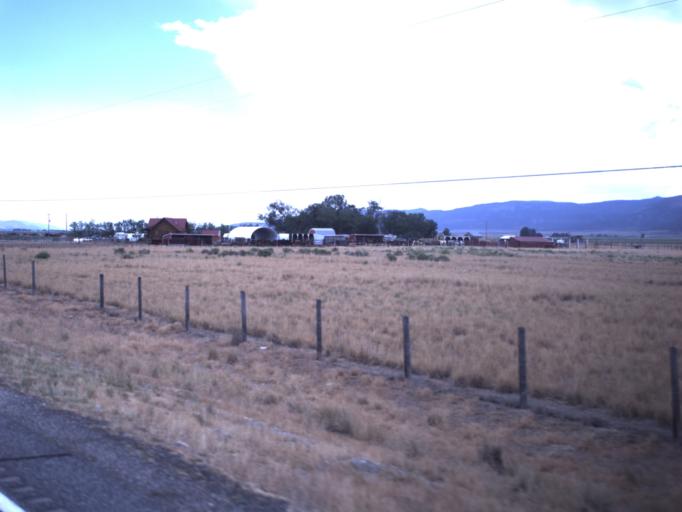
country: US
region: Utah
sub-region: Sanpete County
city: Moroni
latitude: 39.4641
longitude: -111.5627
